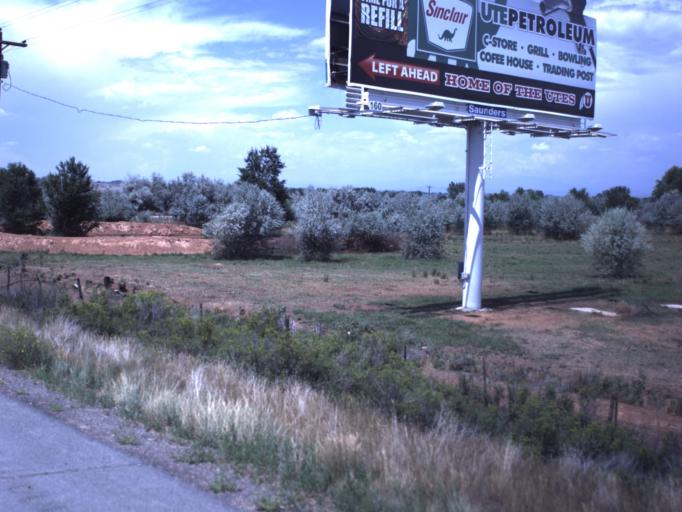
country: US
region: Utah
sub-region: Duchesne County
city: Roosevelt
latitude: 40.3020
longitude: -109.8383
